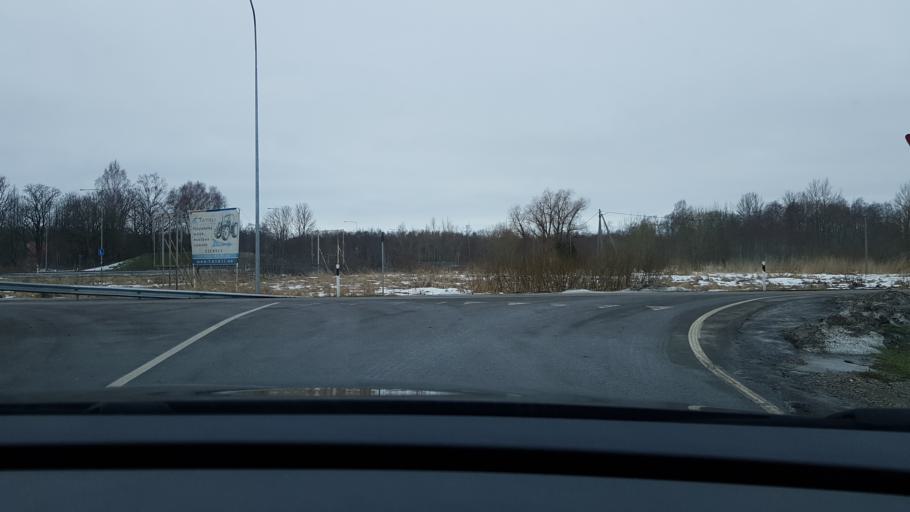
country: EE
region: Paernumaa
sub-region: Sauga vald
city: Sauga
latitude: 58.4487
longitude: 24.5000
